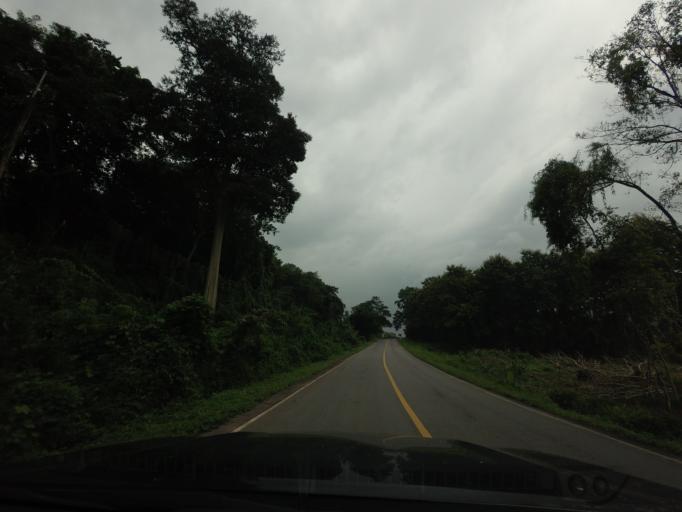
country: TH
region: Nong Khai
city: Sangkhom
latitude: 18.0268
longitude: 102.3645
